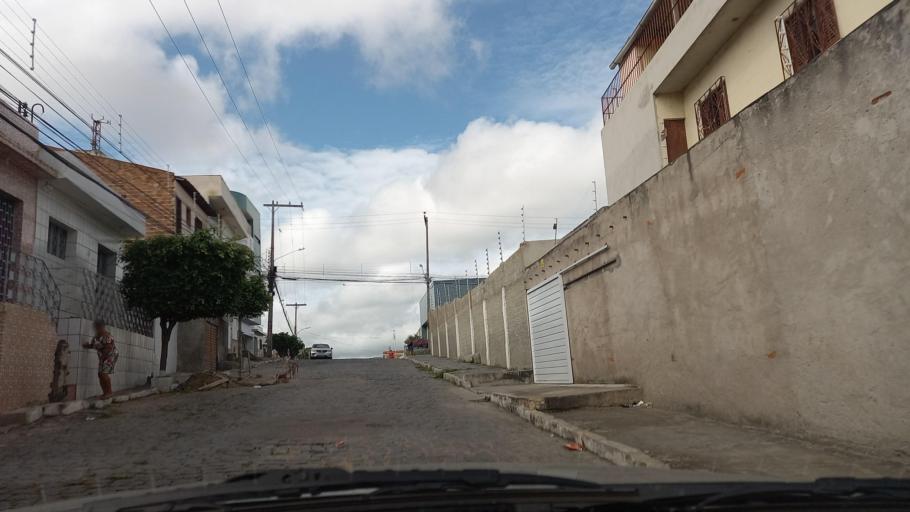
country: BR
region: Pernambuco
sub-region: Caruaru
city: Caruaru
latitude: -8.2849
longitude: -35.9806
